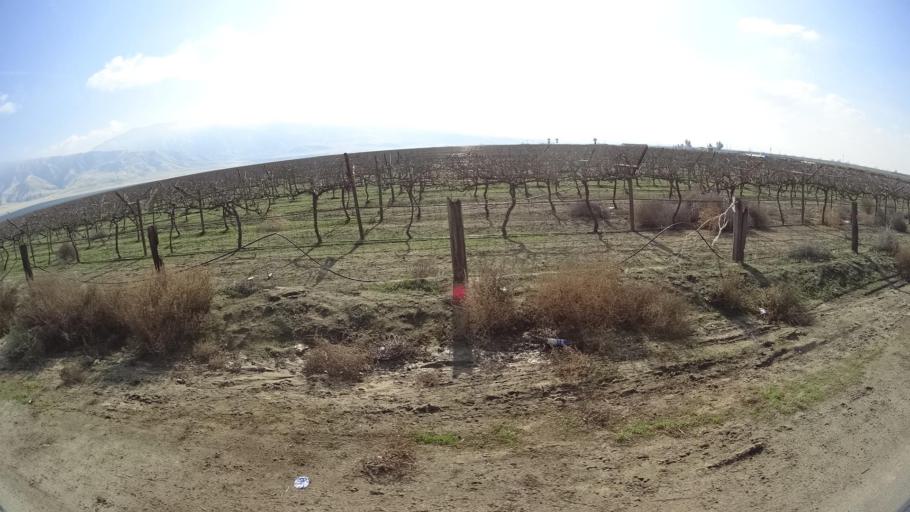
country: US
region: California
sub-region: Kern County
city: Arvin
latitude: 35.2384
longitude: -118.7725
